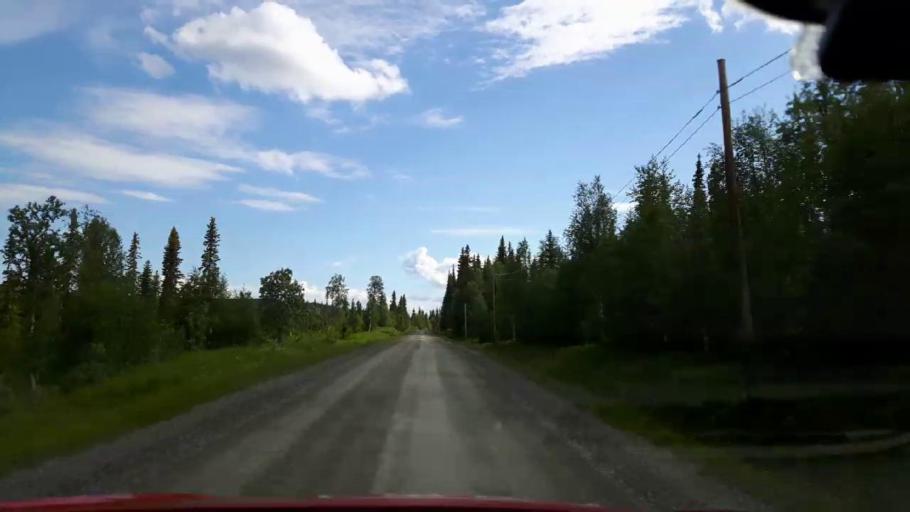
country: SE
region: Jaemtland
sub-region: Krokoms Kommun
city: Valla
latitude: 63.8110
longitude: 14.0494
